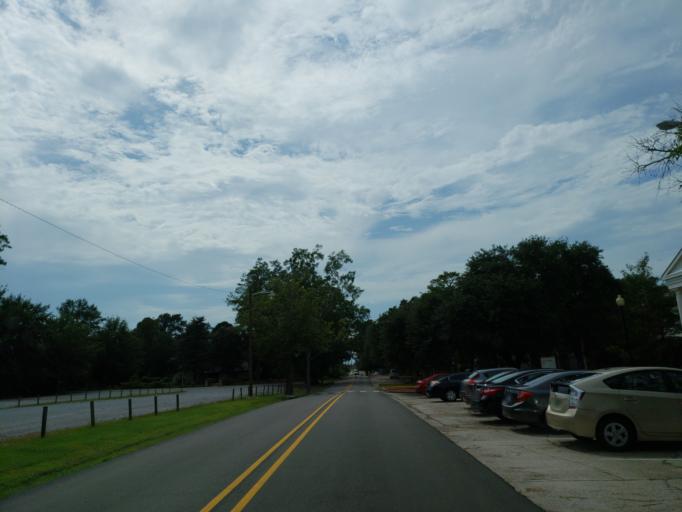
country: US
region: Mississippi
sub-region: Lamar County
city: Arnold Line
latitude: 31.3285
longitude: -89.3421
